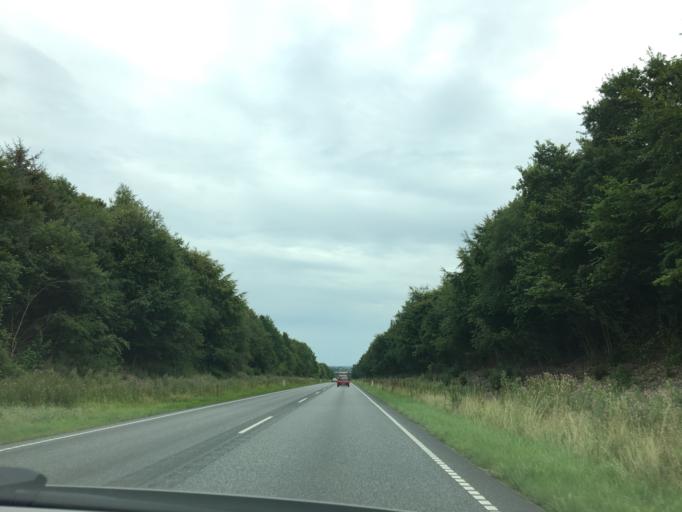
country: DK
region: South Denmark
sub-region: Vejle Kommune
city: Borkop
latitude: 55.6592
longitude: 9.6215
